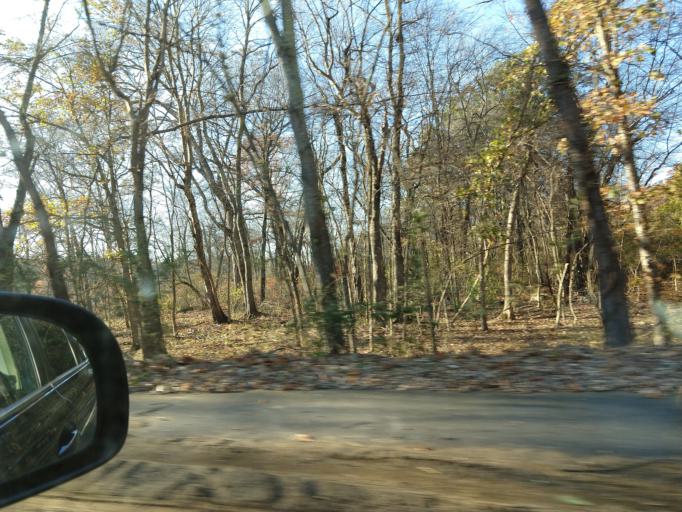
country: US
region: Massachusetts
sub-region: Middlesex County
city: Concord
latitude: 42.4430
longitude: -71.3658
